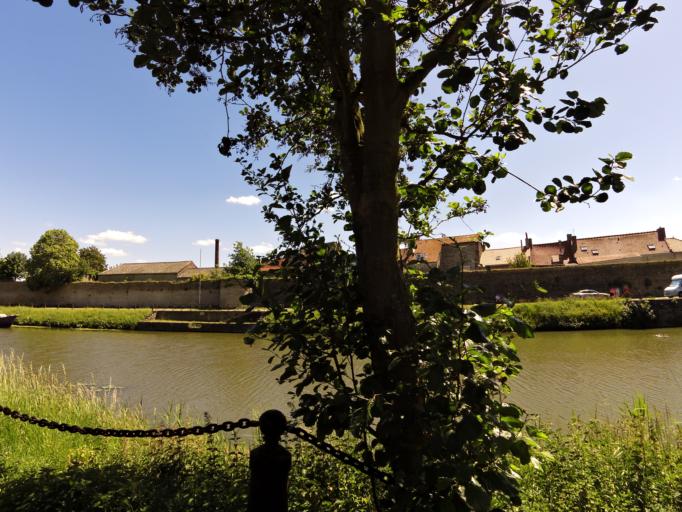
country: FR
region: Nord-Pas-de-Calais
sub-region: Departement du Nord
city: Bergues
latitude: 50.9717
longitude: 2.4277
